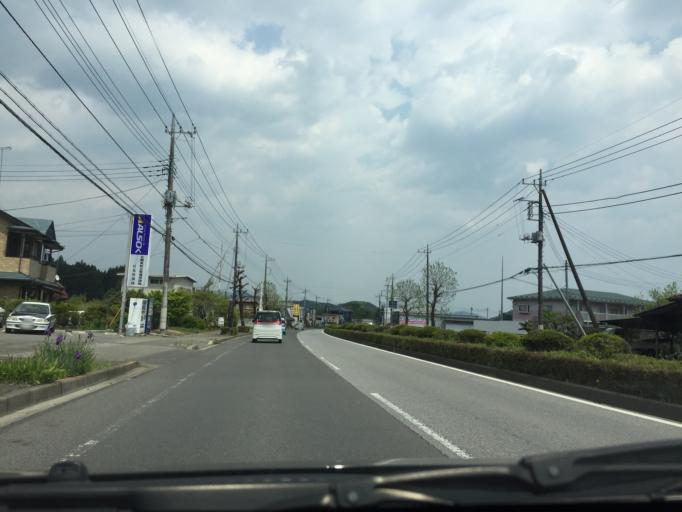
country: JP
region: Tochigi
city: Imaichi
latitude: 36.7399
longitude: 139.6988
